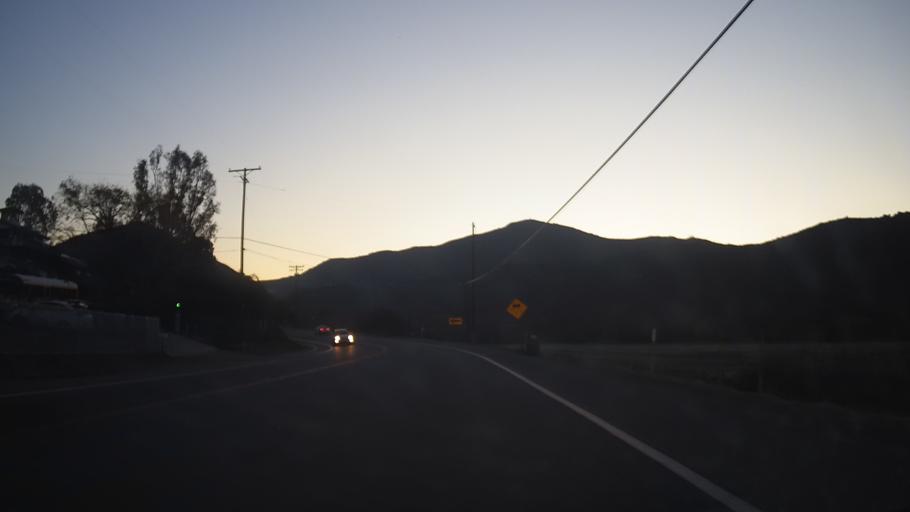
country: US
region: California
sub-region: San Diego County
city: Crest
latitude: 32.7811
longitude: -116.8503
